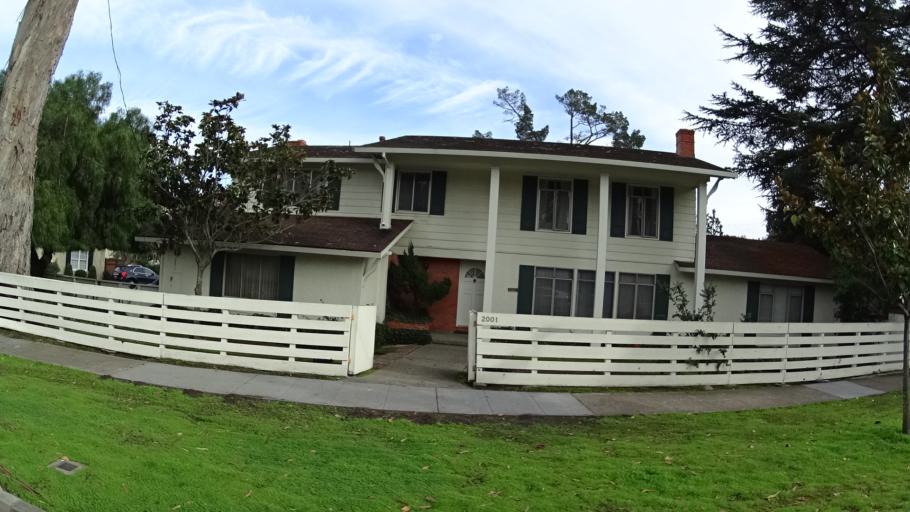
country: US
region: California
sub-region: San Mateo County
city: Burlingame
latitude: 37.5818
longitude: -122.3718
